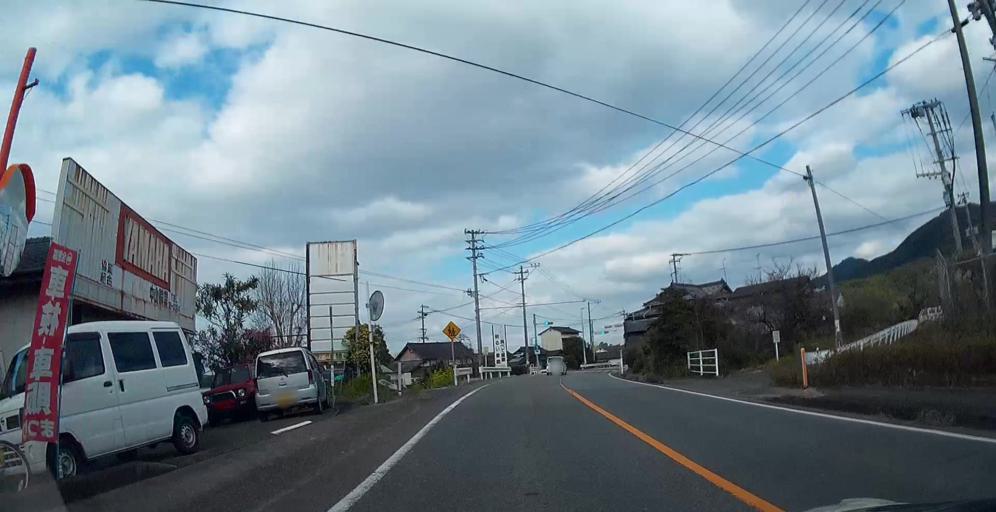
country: JP
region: Kumamoto
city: Yatsushiro
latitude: 32.4517
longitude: 130.5923
